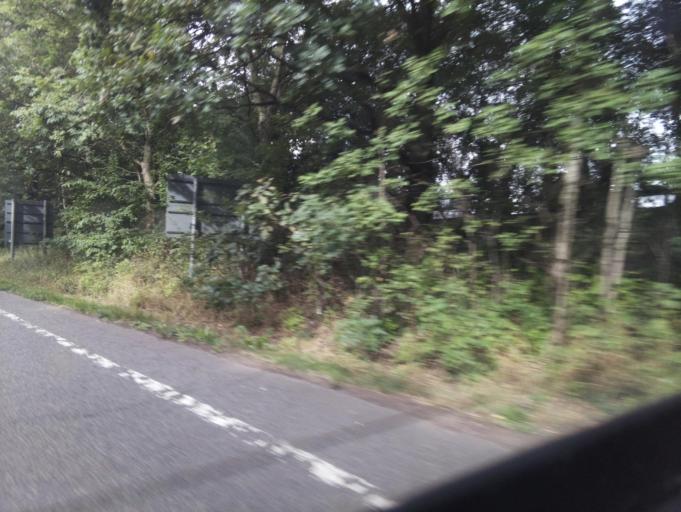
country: GB
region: England
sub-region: Telford and Wrekin
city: Newport
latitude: 52.7724
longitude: -2.3629
